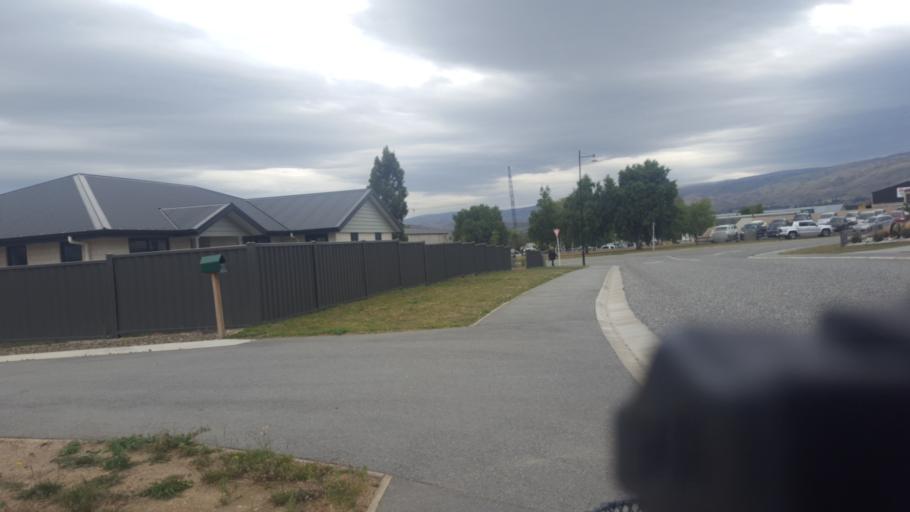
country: NZ
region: Otago
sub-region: Queenstown-Lakes District
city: Wanaka
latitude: -45.0483
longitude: 169.1825
